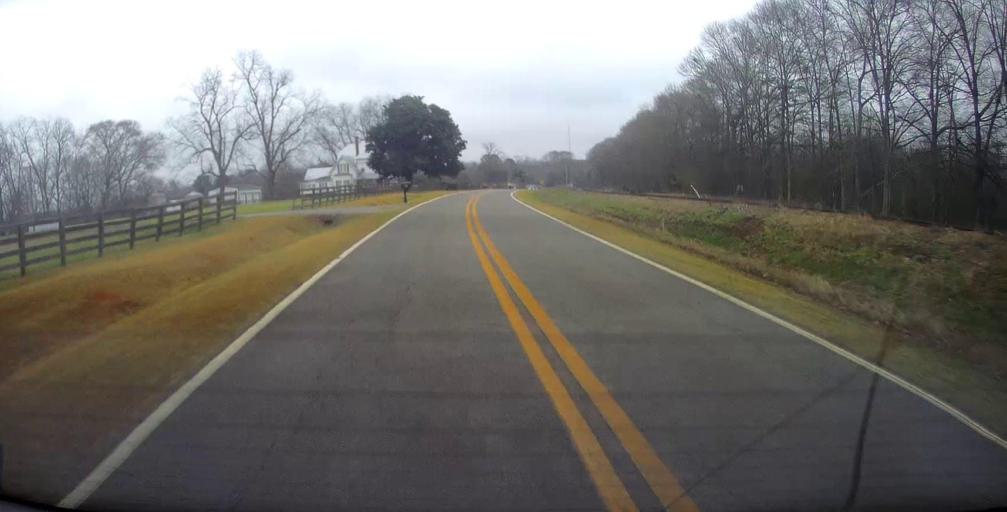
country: US
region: Georgia
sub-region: Lamar County
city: Barnesville
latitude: 33.0769
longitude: -84.0960
